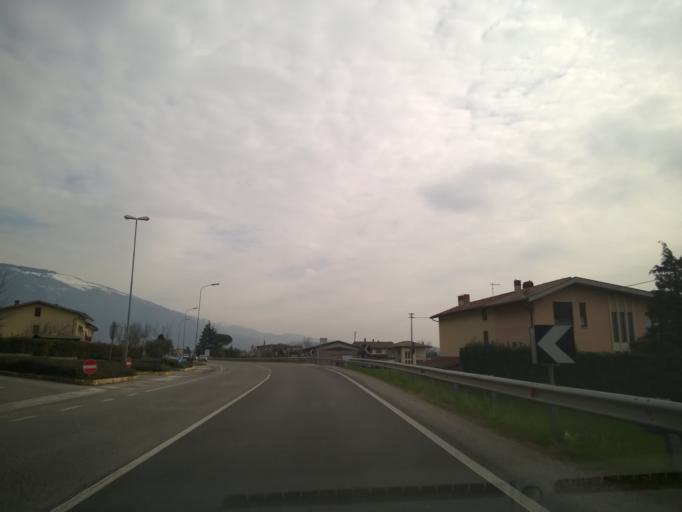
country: IT
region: Veneto
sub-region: Provincia di Vicenza
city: Santorso
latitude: 45.7380
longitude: 11.4086
